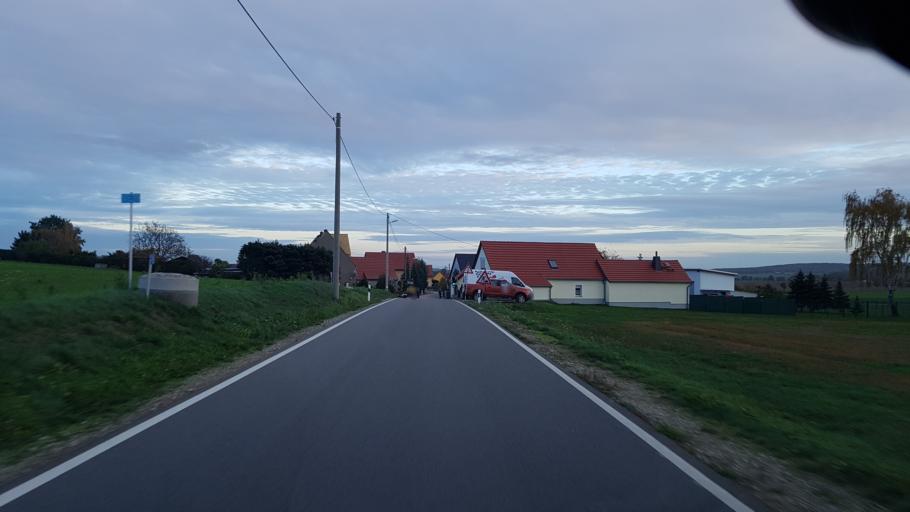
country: DE
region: Saxony
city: Cavertitz
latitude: 51.4030
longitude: 13.1239
